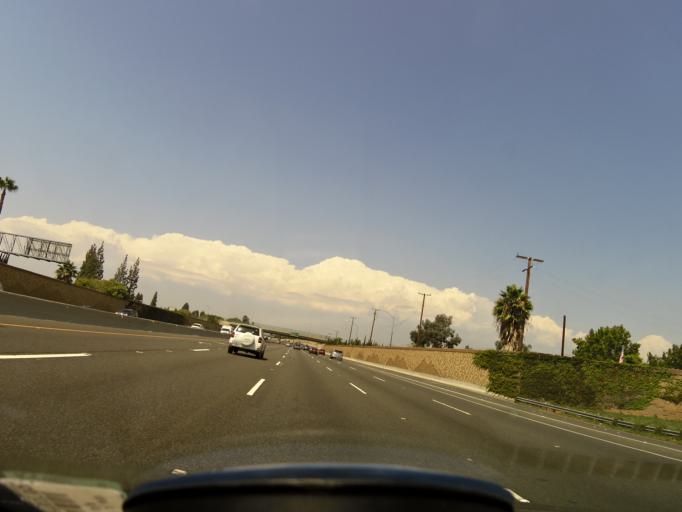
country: US
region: California
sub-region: Orange County
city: Orange
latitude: 33.7911
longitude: -117.8309
